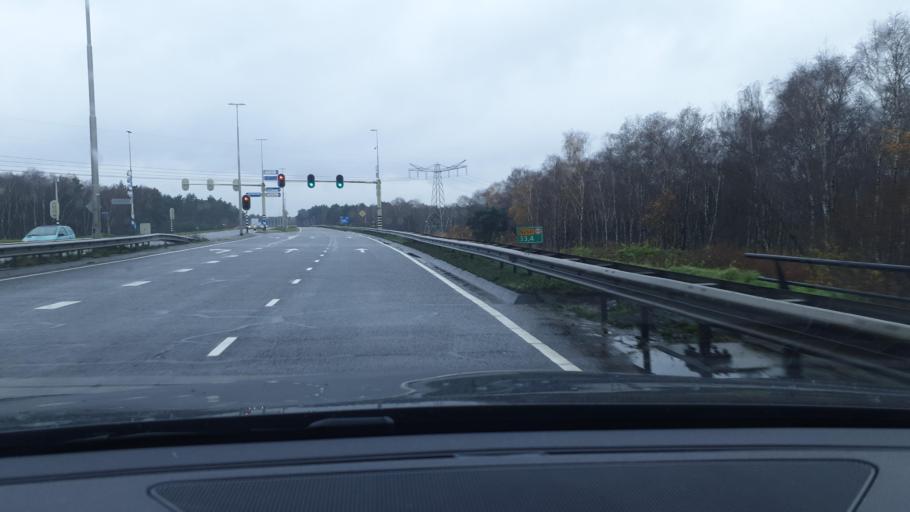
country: NL
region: North Brabant
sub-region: Gemeente Loon op Zand
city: Loon op Zand
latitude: 51.5978
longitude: 5.0671
